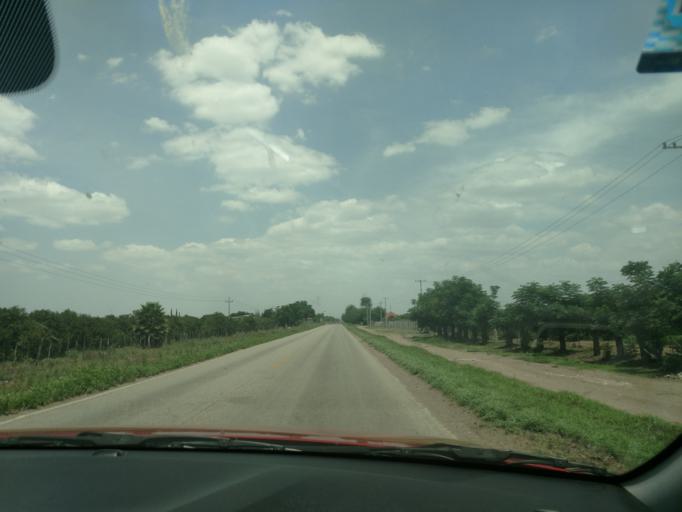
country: MX
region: San Luis Potosi
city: Ciudad Fernandez
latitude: 21.9541
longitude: -100.0690
